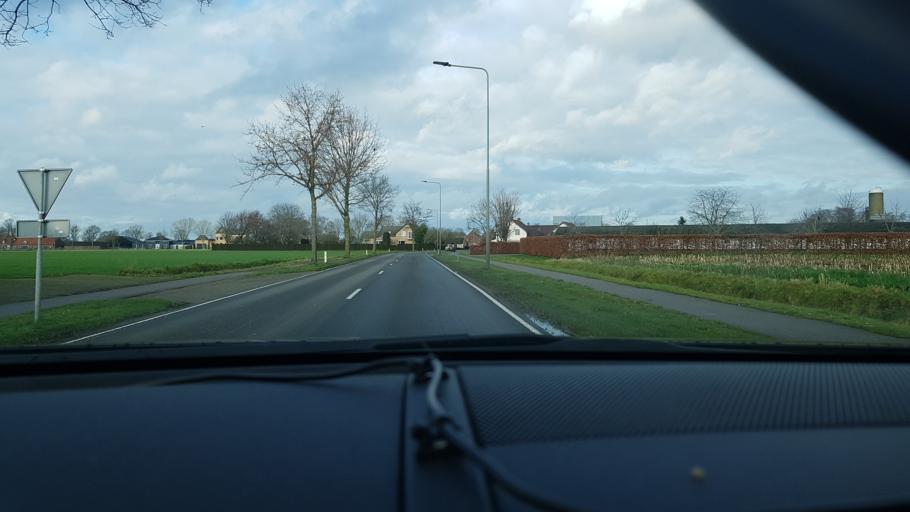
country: NL
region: Limburg
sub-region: Gemeente Nederweert
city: Nederweert
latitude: 51.2824
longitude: 5.7699
